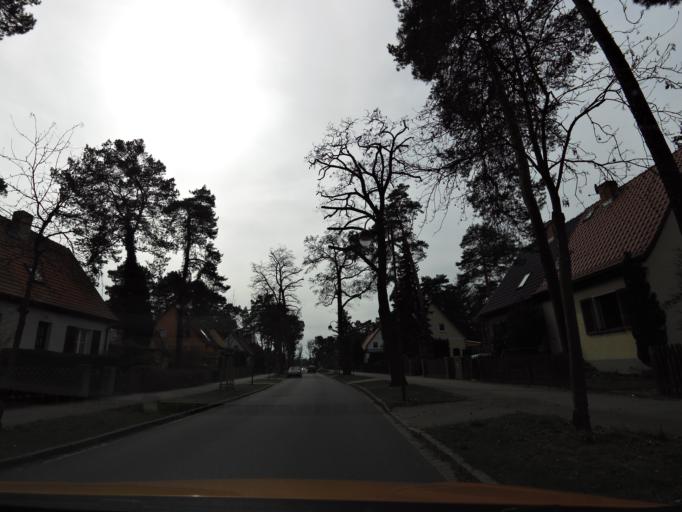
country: DE
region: Brandenburg
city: Rangsdorf
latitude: 52.3346
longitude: 13.4111
